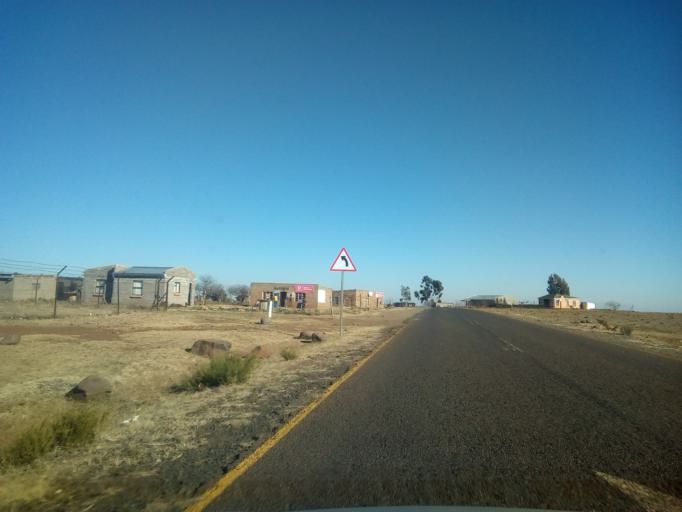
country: LS
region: Berea
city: Teyateyaneng
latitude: -29.2521
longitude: 27.7358
